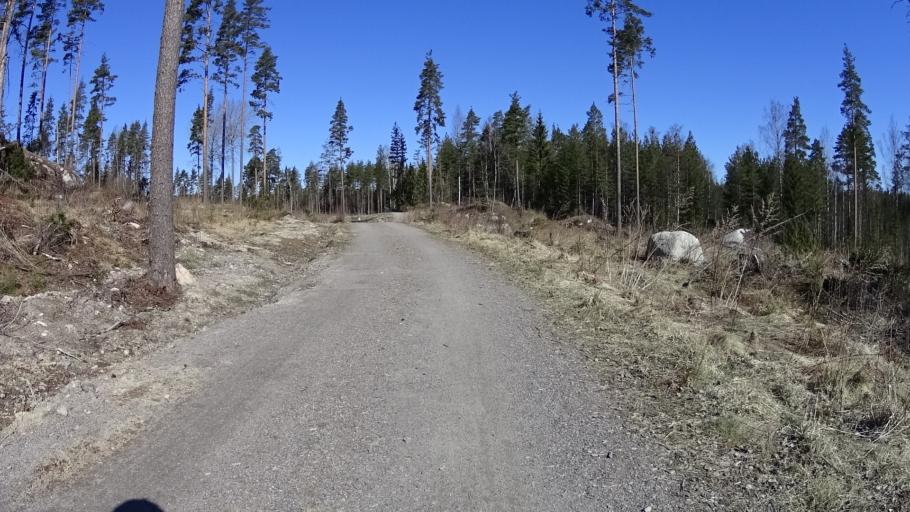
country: FI
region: Uusimaa
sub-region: Helsinki
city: Espoo
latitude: 60.2381
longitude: 24.6291
